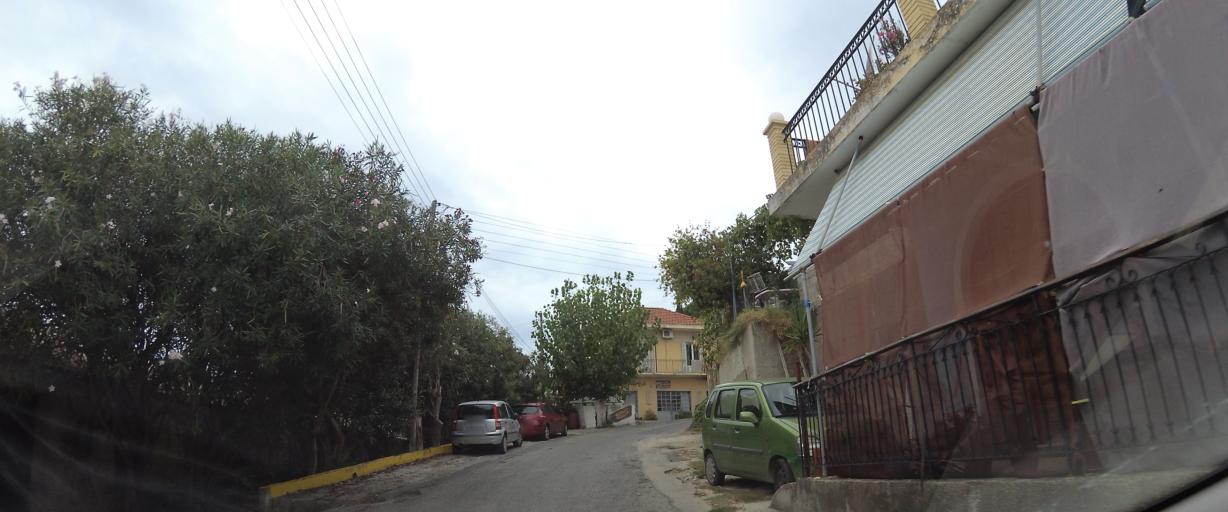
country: GR
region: Ionian Islands
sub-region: Nomos Kerkyras
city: Agios Georgis
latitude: 39.7465
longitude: 19.6807
